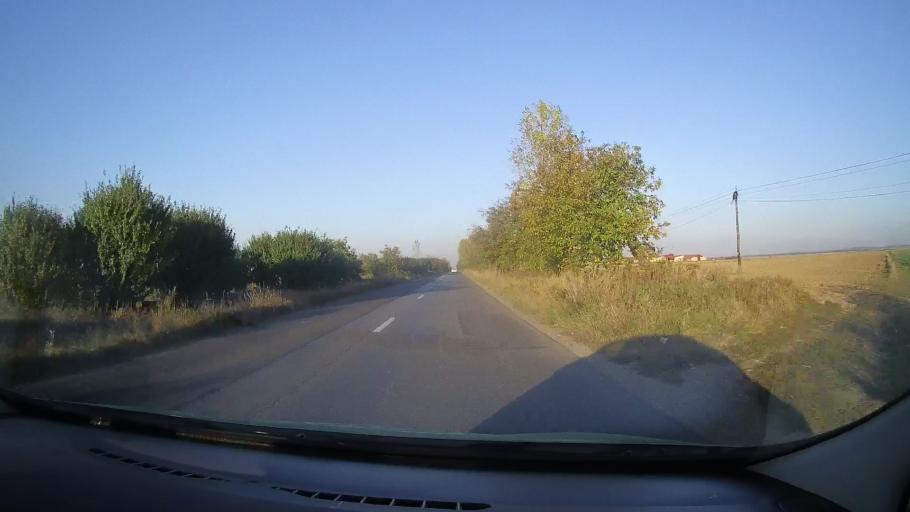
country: RO
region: Bihor
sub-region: Comuna Biharea
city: Biharea
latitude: 47.1699
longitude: 21.9558
